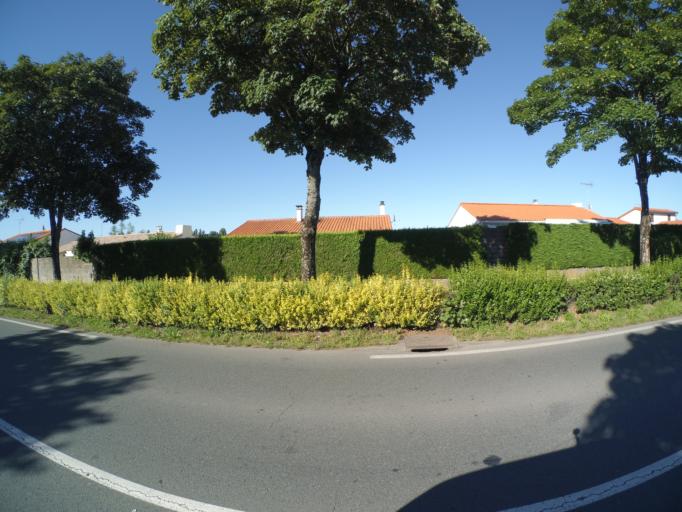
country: FR
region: Pays de la Loire
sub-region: Departement de la Vendee
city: Les Herbiers
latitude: 46.8656
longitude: -1.0247
